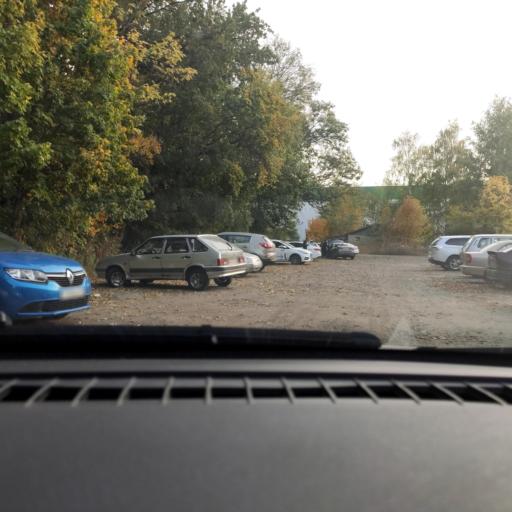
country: RU
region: Voronezj
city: Podgornoye
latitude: 51.8087
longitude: 39.2230
